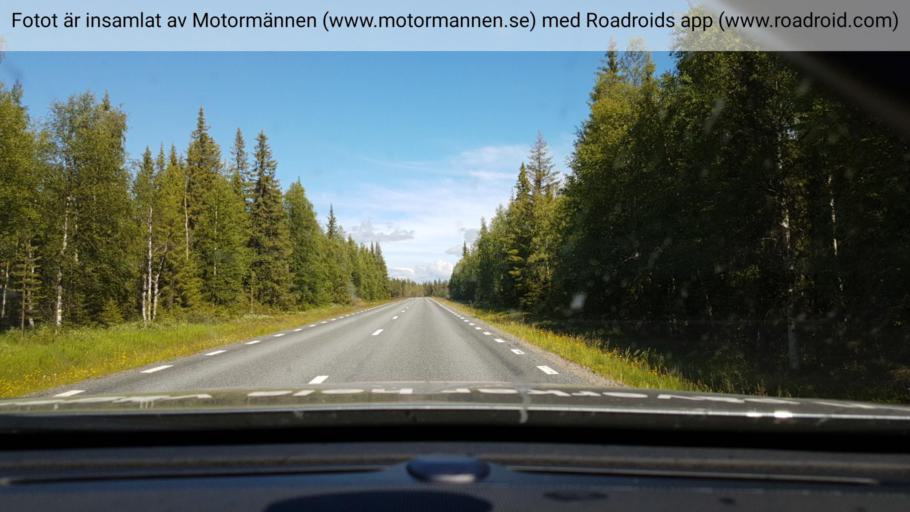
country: SE
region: Vaesterbotten
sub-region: Sorsele Kommun
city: Sorsele
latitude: 65.5685
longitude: 18.0179
